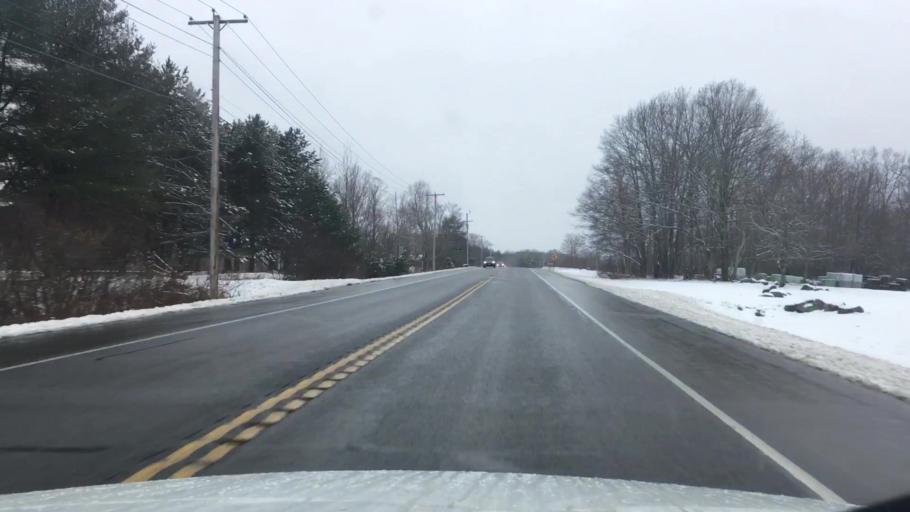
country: US
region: Maine
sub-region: Knox County
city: Rockport
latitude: 44.1575
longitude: -69.1154
